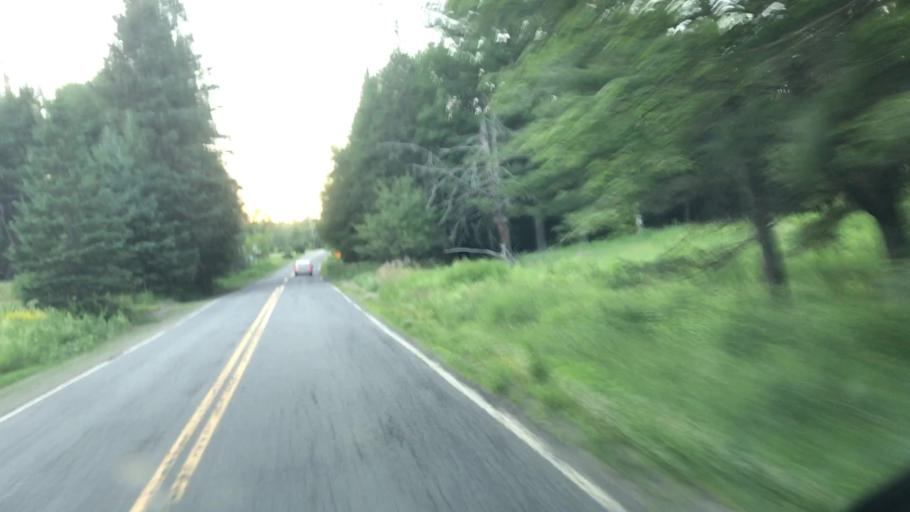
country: US
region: Maine
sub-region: Penobscot County
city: Medway
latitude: 45.6097
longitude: -68.2575
